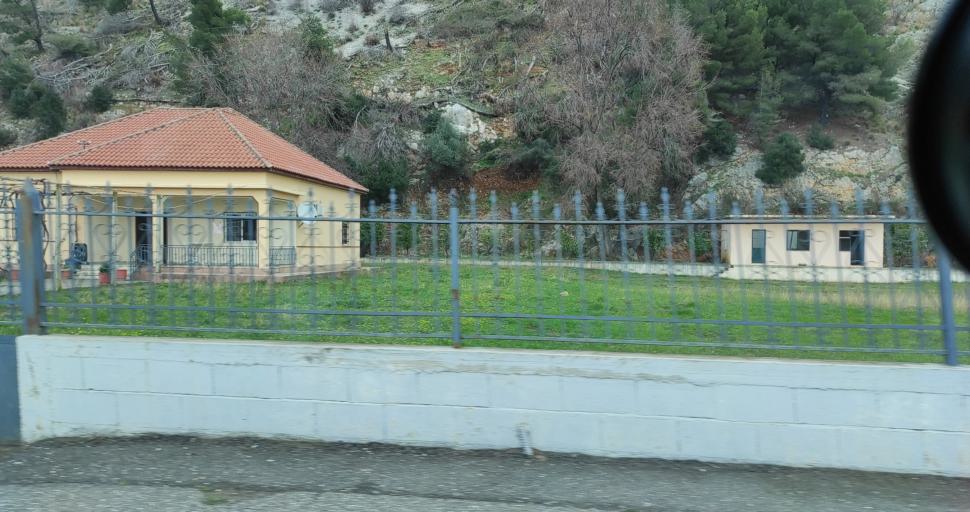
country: AL
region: Lezhe
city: Lezhe
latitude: 41.7958
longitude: 19.6204
